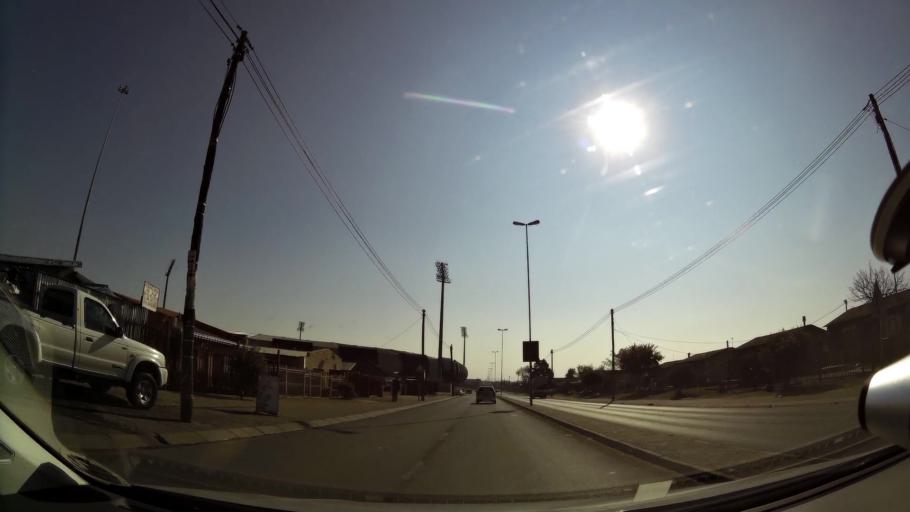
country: ZA
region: Orange Free State
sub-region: Mangaung Metropolitan Municipality
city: Bloemfontein
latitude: -29.1763
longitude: 26.2339
